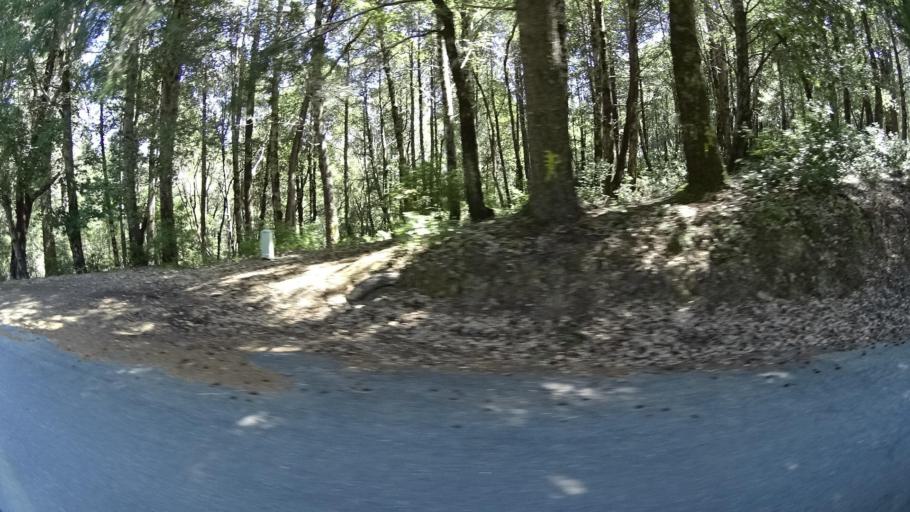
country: US
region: California
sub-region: Humboldt County
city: Redway
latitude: 40.0932
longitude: -123.9501
